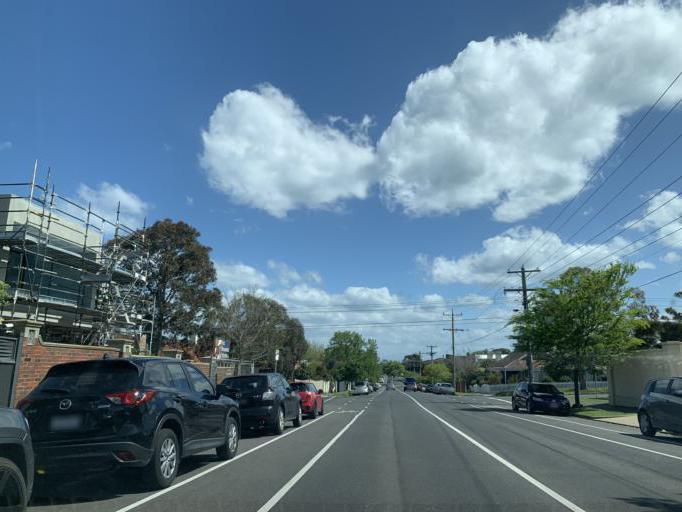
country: AU
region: Victoria
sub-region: Bayside
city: North Brighton
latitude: -37.9097
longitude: 144.9967
